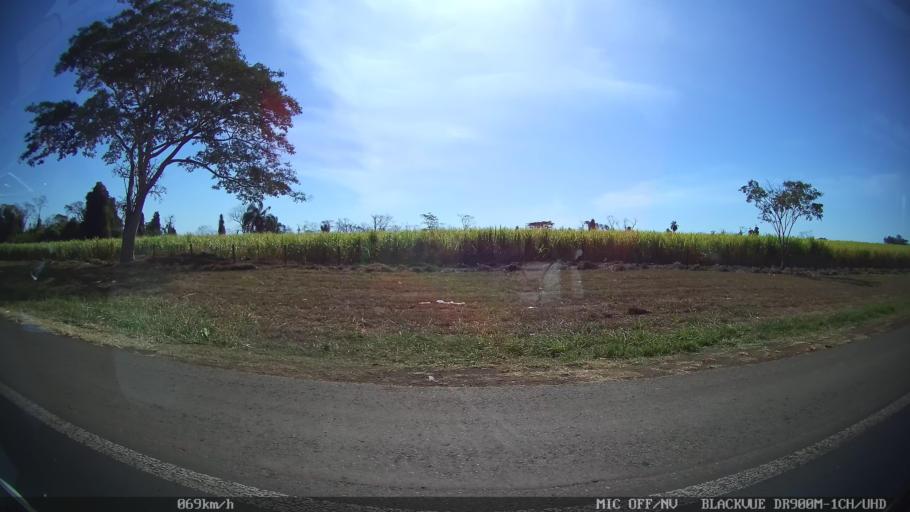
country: BR
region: Sao Paulo
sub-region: Barretos
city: Barretos
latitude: -20.5731
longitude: -48.6753
